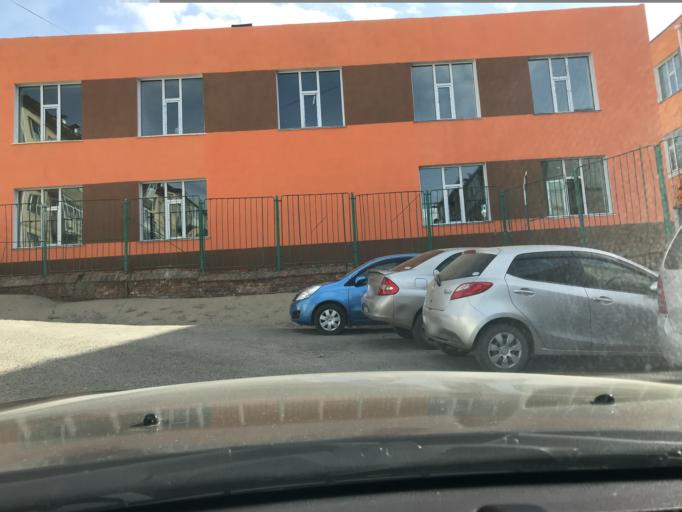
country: MN
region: Ulaanbaatar
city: Ulaanbaatar
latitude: 47.9229
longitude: 106.9449
